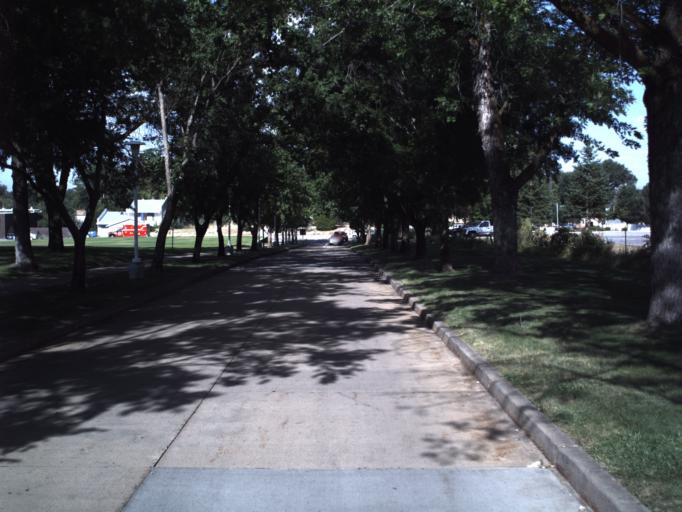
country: US
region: Utah
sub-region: Weber County
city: Harrisville
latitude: 41.2645
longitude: -111.9676
